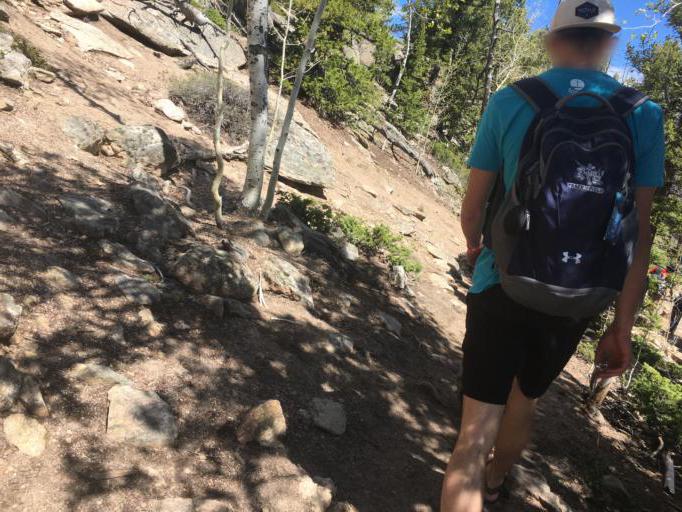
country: US
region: Colorado
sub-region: Larimer County
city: Estes Park
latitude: 40.3198
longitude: -105.5406
